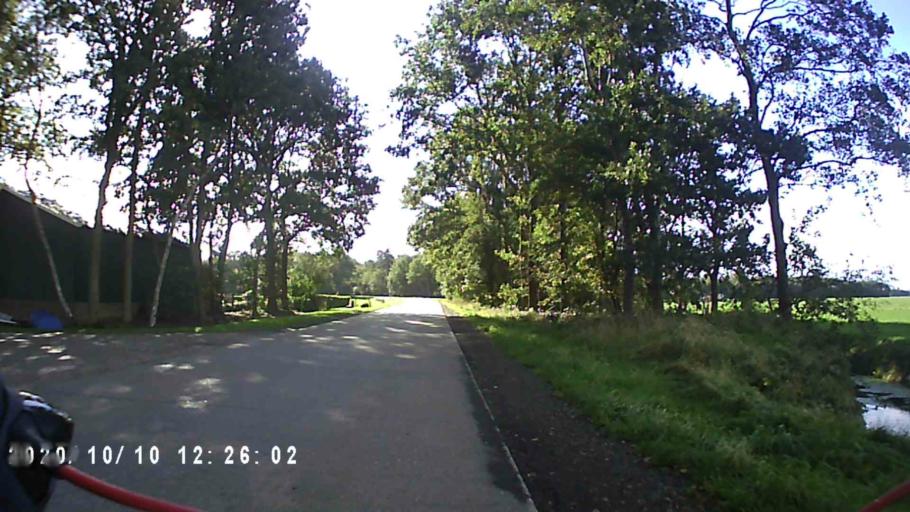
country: NL
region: Friesland
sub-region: Gemeente Heerenveen
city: Jubbega
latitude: 52.9867
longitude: 6.1798
